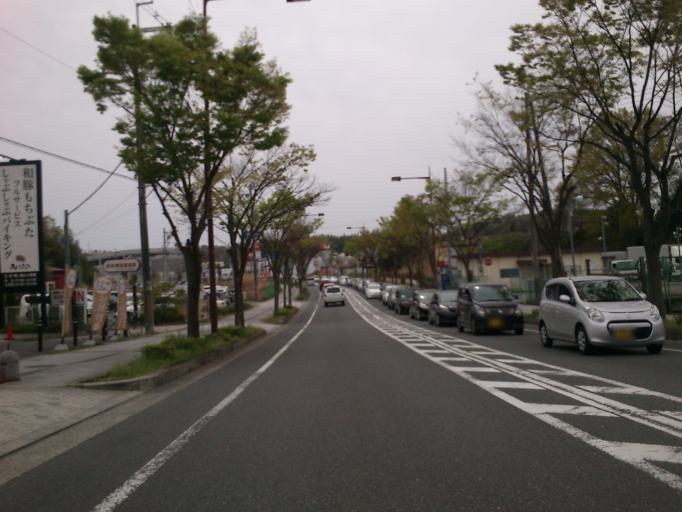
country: JP
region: Kyoto
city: Yawata
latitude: 34.8447
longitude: 135.7131
